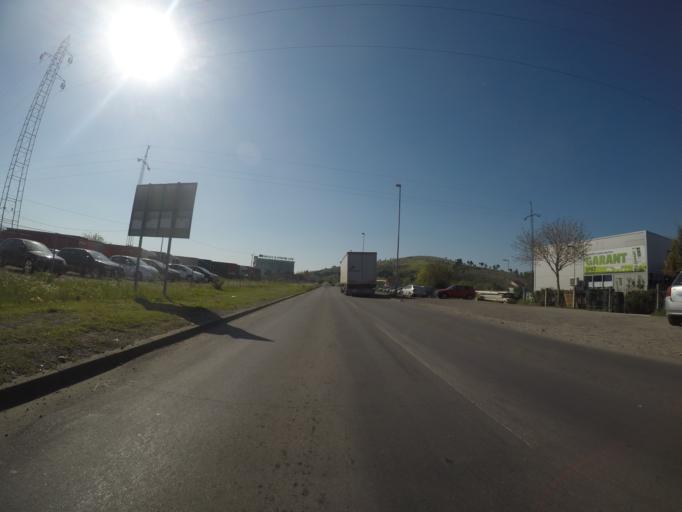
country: ME
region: Podgorica
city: Podgorica
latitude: 42.4282
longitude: 19.2328
